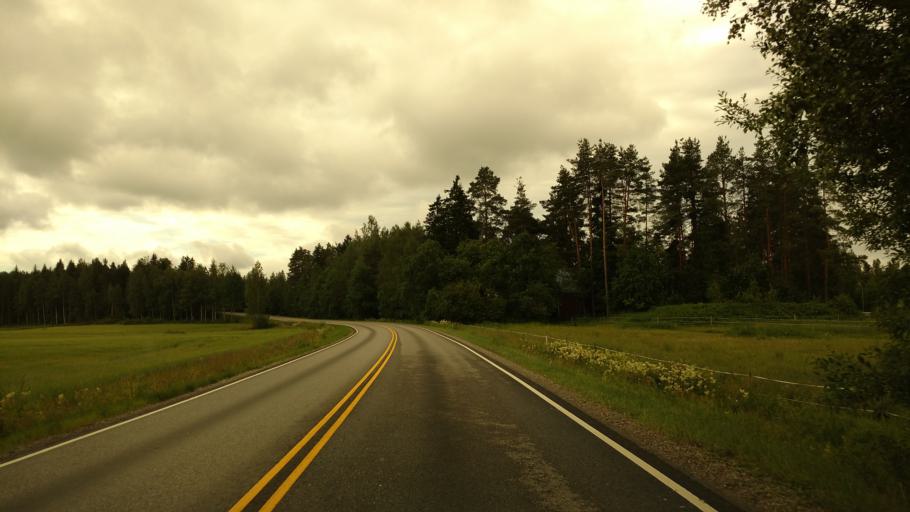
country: FI
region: Varsinais-Suomi
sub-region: Salo
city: Kuusjoki
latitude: 60.4464
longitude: 23.1761
